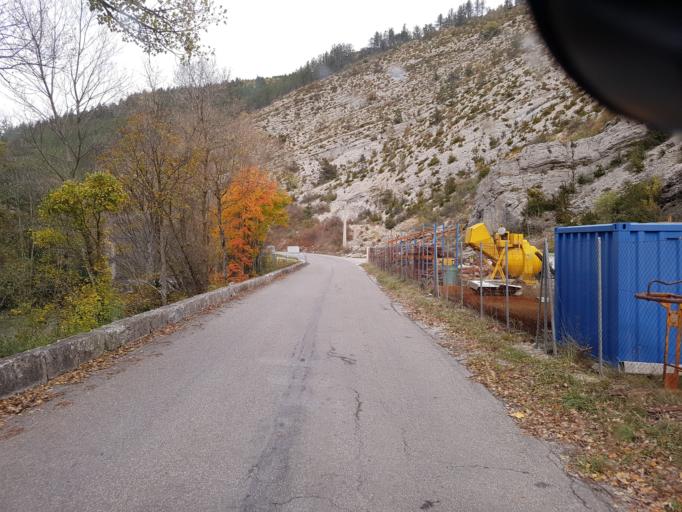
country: FR
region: Provence-Alpes-Cote d'Azur
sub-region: Departement des Hautes-Alpes
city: Serres
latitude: 44.3137
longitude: 5.6888
